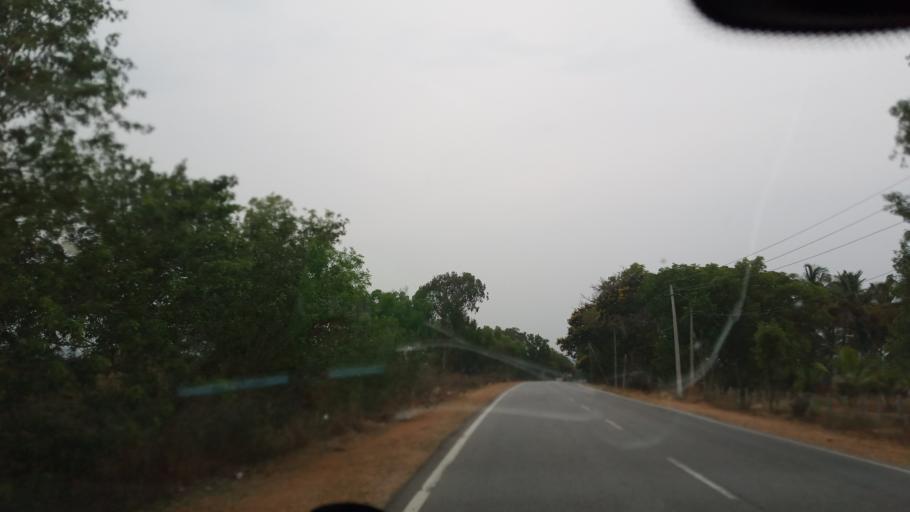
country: IN
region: Karnataka
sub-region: Mandya
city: Belluru
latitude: 12.9526
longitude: 76.7539
